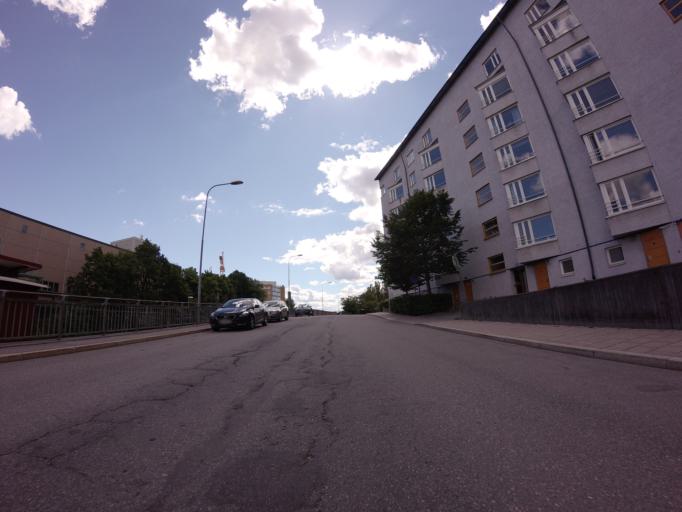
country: SE
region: Stockholm
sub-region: Stockholms Kommun
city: Stockholm
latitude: 59.3510
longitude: 18.0644
